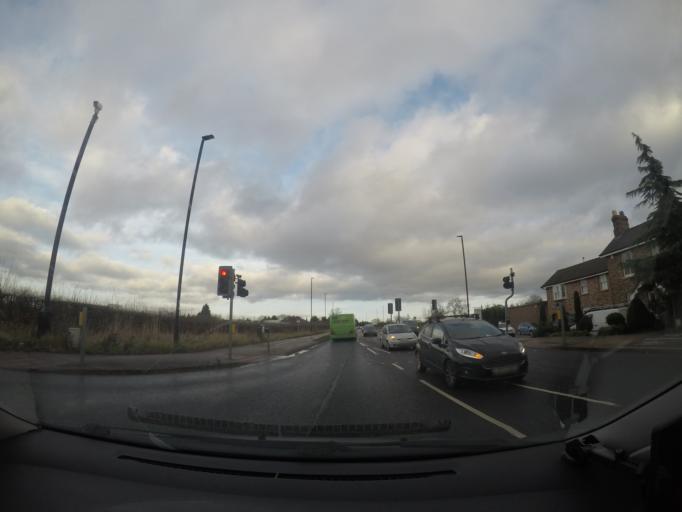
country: GB
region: England
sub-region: City of York
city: Huntington
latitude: 53.9775
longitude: -1.0537
